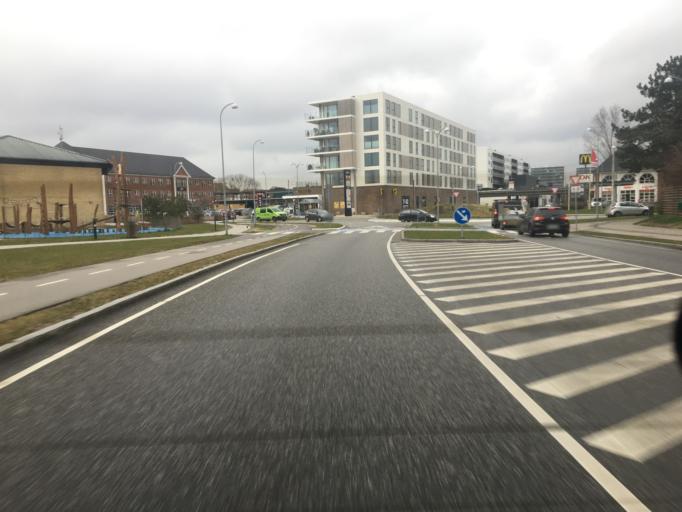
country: DK
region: Capital Region
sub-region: Vallensbaek Kommune
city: Vallensbaek
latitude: 55.6219
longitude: 12.3902
